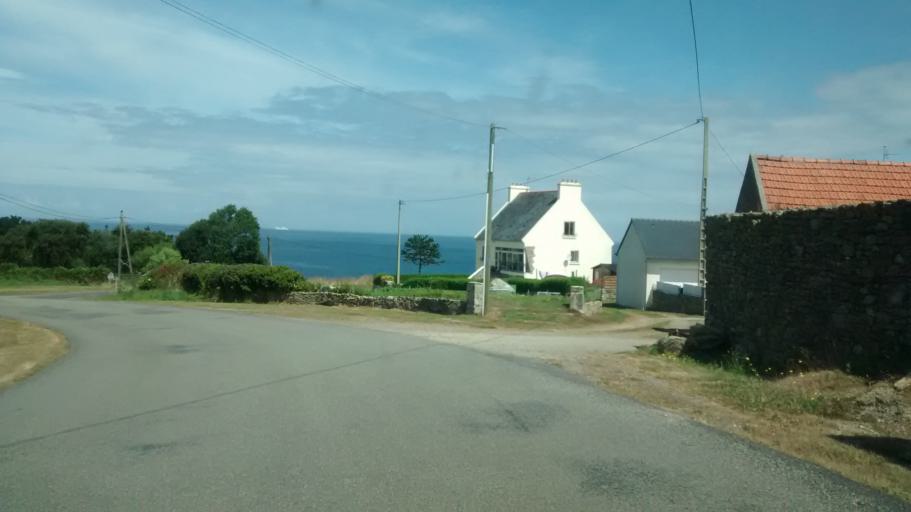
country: FR
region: Brittany
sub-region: Departement du Finistere
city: Plouguerneau
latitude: 48.6206
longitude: -4.4796
